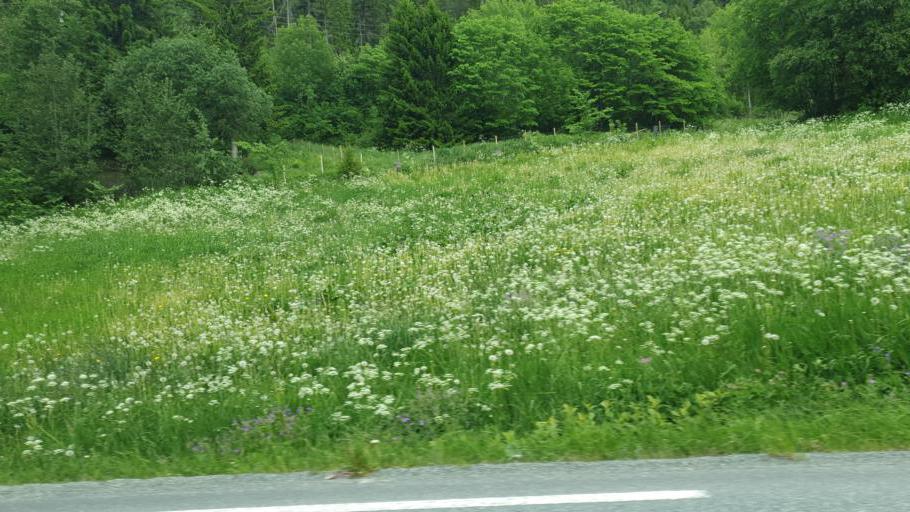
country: NO
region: Sor-Trondelag
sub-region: Trondheim
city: Trondheim
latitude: 63.5572
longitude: 10.2982
